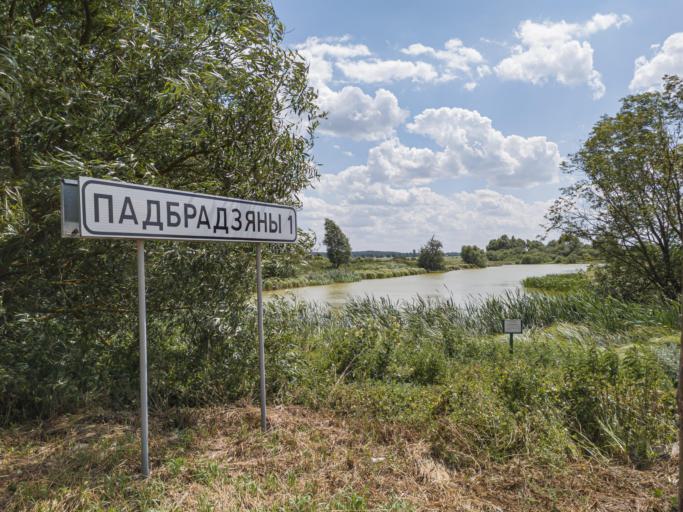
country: BY
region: Brest
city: Kamyanyets
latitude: 52.3719
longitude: 23.8957
